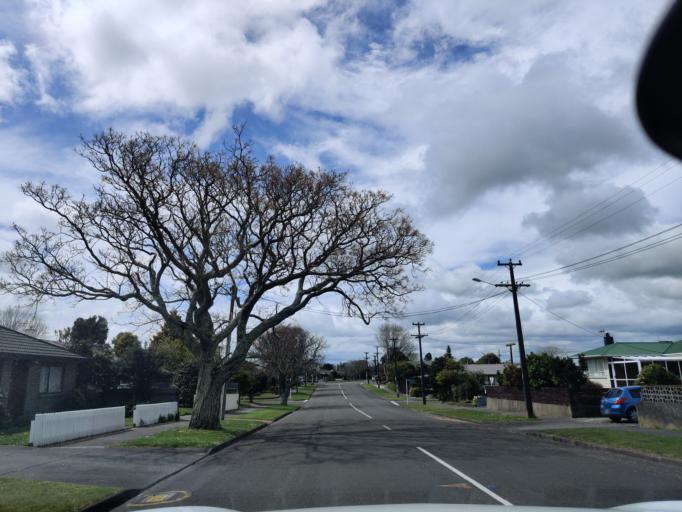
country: NZ
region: Manawatu-Wanganui
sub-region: Palmerston North City
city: Palmerston North
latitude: -40.3812
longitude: 175.5864
